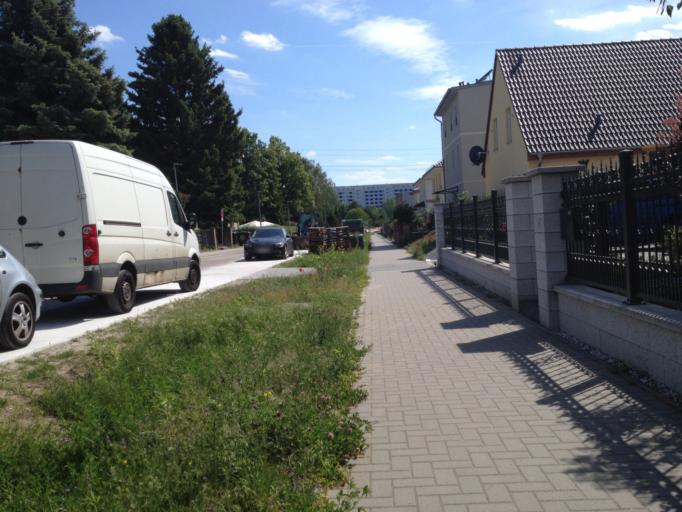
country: DE
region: Berlin
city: Friedrichsfelde
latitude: 52.5176
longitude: 13.5273
